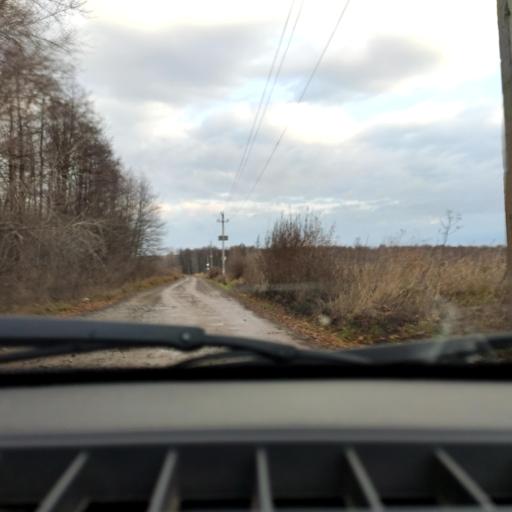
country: RU
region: Bashkortostan
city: Avdon
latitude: 54.6309
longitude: 55.7337
